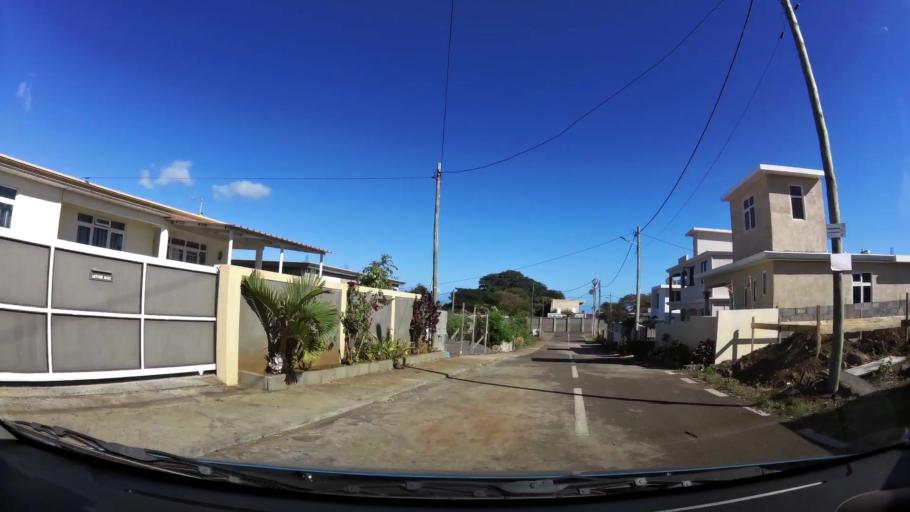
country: MU
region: Black River
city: Cascavelle
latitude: -20.2880
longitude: 57.4046
